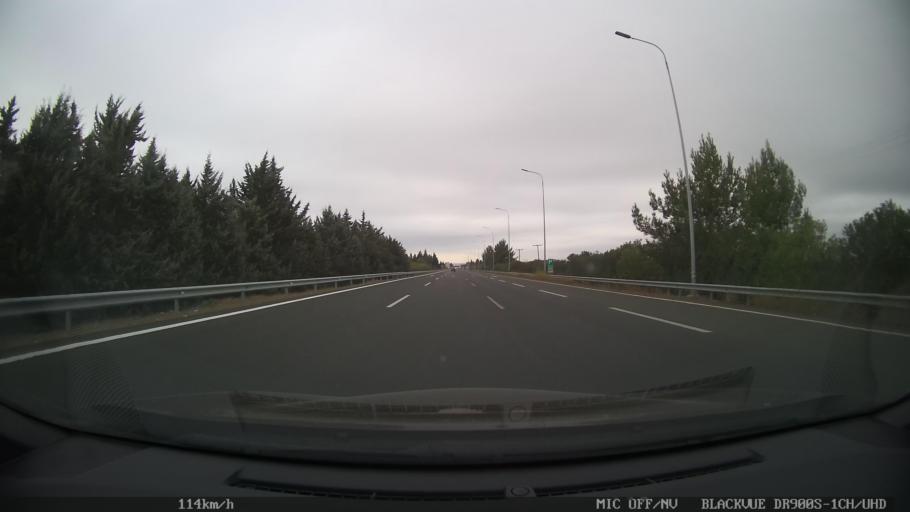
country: GR
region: Central Macedonia
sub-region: Nomos Imathias
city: Kleidi
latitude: 40.5531
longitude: 22.5962
